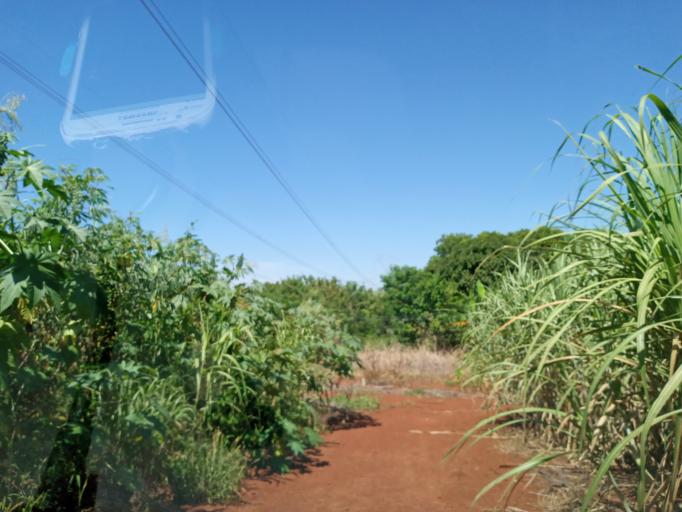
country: BR
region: Goias
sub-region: Itumbiara
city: Itumbiara
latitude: -18.4447
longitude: -49.1399
